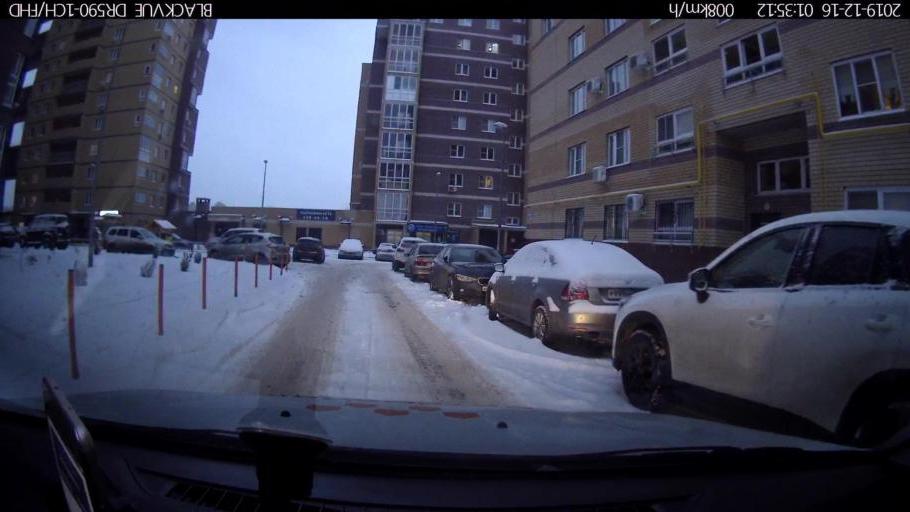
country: RU
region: Nizjnij Novgorod
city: Nizhniy Novgorod
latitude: 56.3080
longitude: 44.0315
